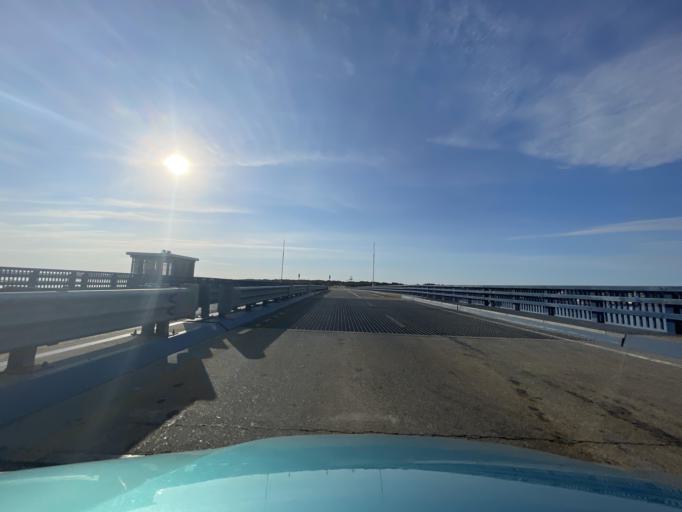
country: US
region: Massachusetts
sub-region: Bristol County
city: Head of Westport
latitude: 41.5176
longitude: -71.0681
